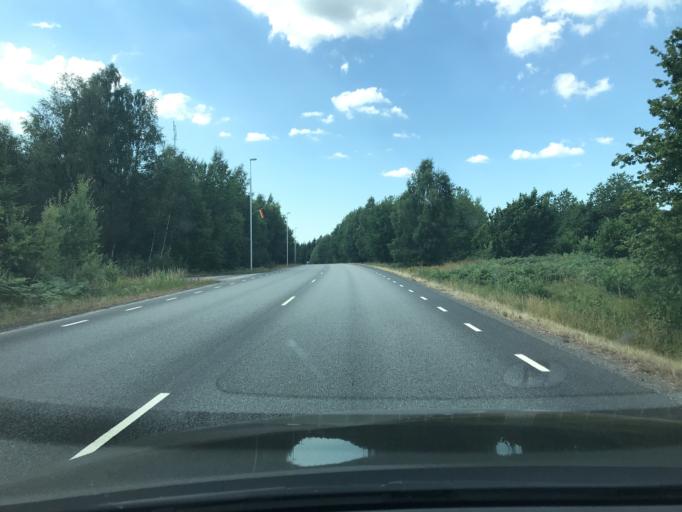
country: SE
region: Skane
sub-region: Hassleholms Kommun
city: Hastveda
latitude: 56.2738
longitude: 13.9508
